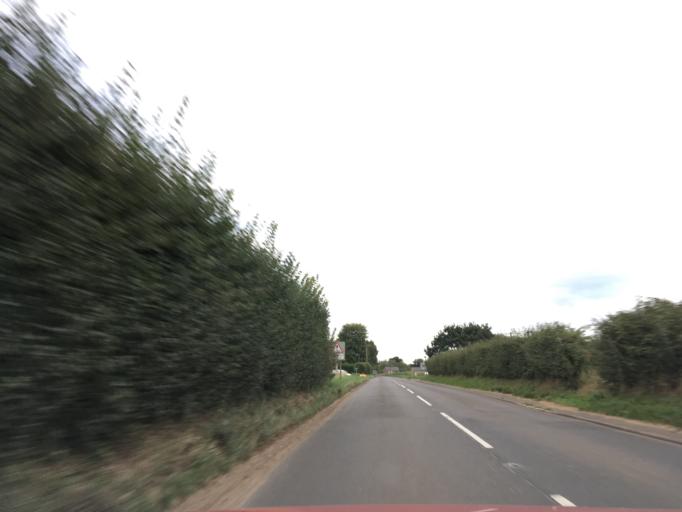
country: GB
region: England
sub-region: Wiltshire
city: Devizes
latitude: 51.3856
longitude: -2.0397
